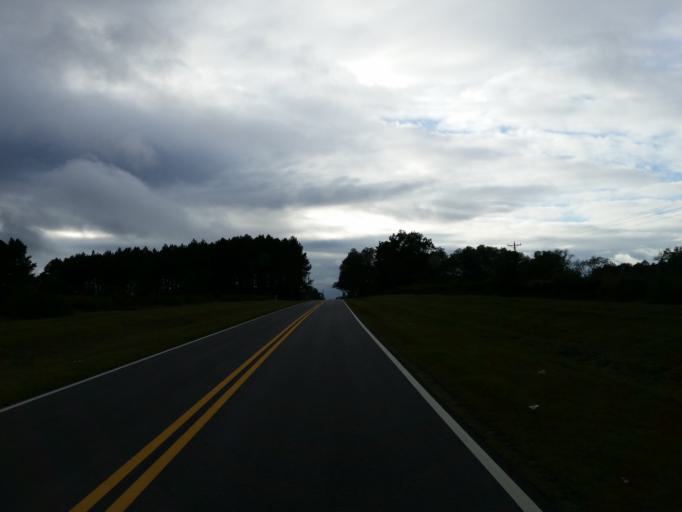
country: US
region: Georgia
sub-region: Tift County
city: Tifton
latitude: 31.5695
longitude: -83.5630
